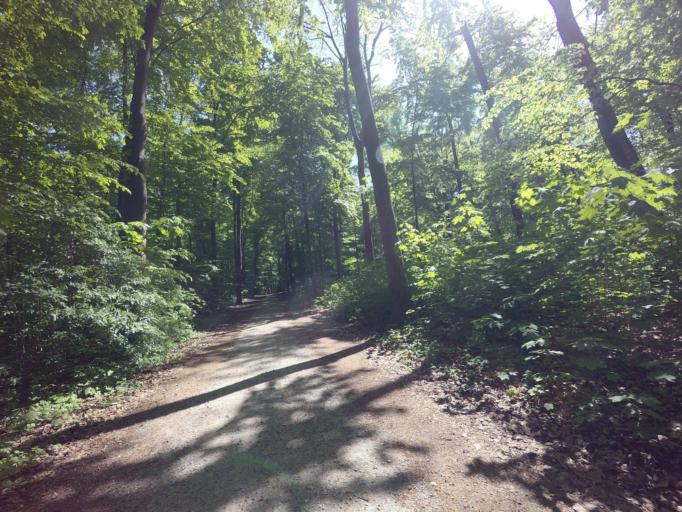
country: DE
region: Lower Saxony
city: Hildesheim
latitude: 52.1392
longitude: 9.9864
